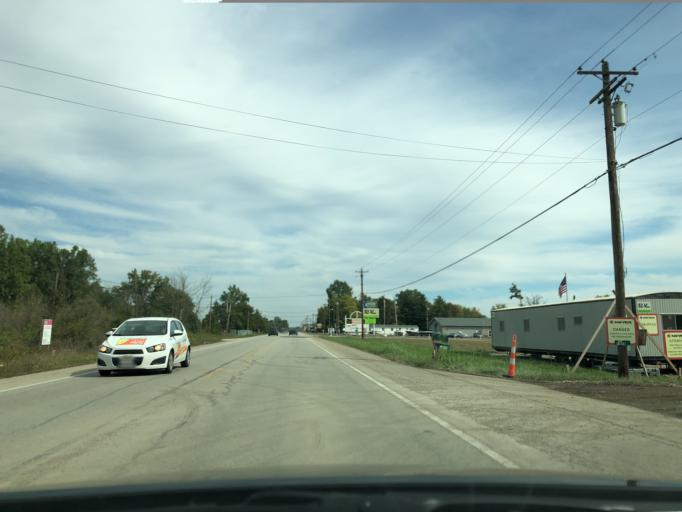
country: US
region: Ohio
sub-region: Clermont County
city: Mount Repose
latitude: 39.2129
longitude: -84.2043
